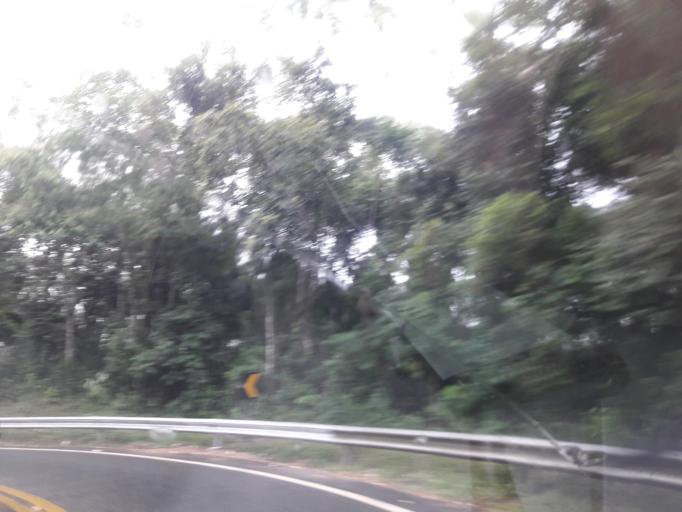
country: BR
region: Sao Paulo
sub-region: Aruja
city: Aruja
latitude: -23.2994
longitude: -46.4289
